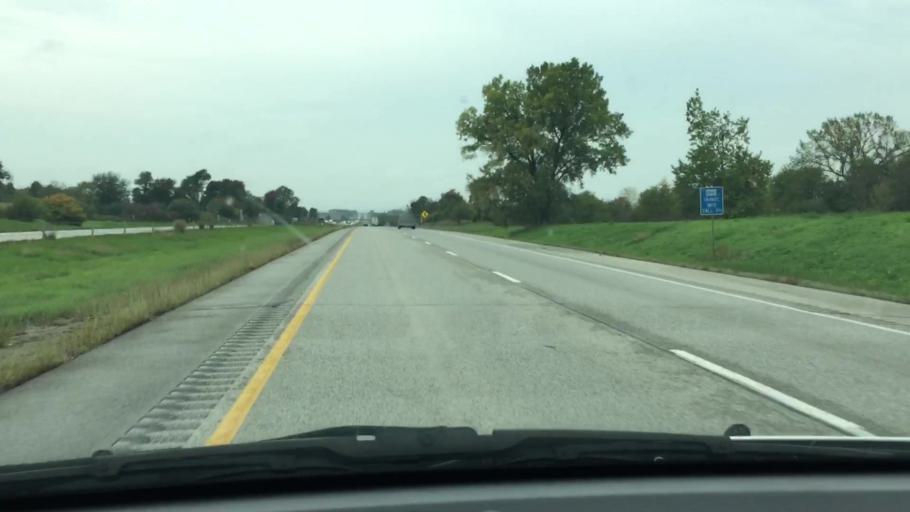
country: US
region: Iowa
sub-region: Johnson County
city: Tiffin
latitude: 41.6940
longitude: -91.6674
